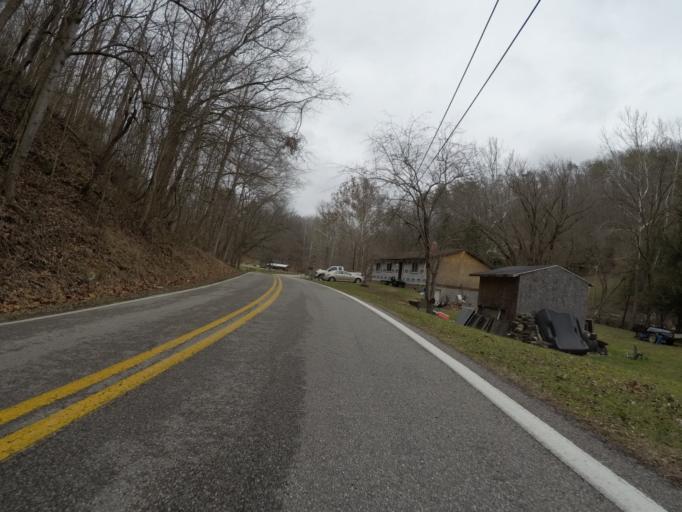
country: US
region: West Virginia
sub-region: Cabell County
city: Barboursville
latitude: 38.4422
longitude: -82.2455
